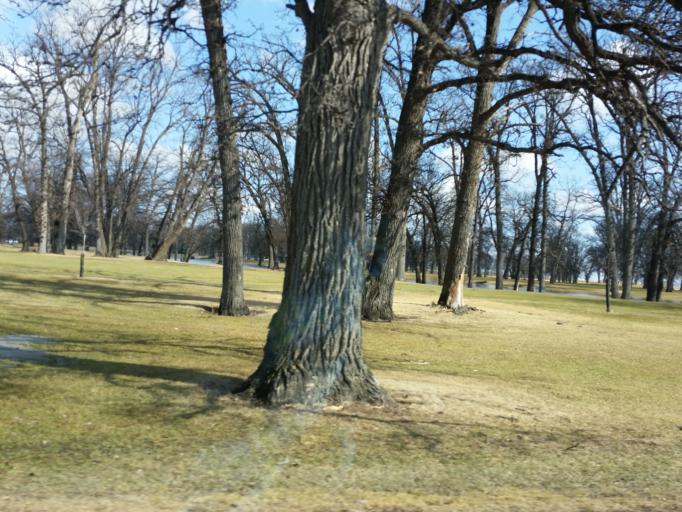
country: US
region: North Dakota
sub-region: Walsh County
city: Grafton
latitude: 48.4213
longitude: -97.3916
